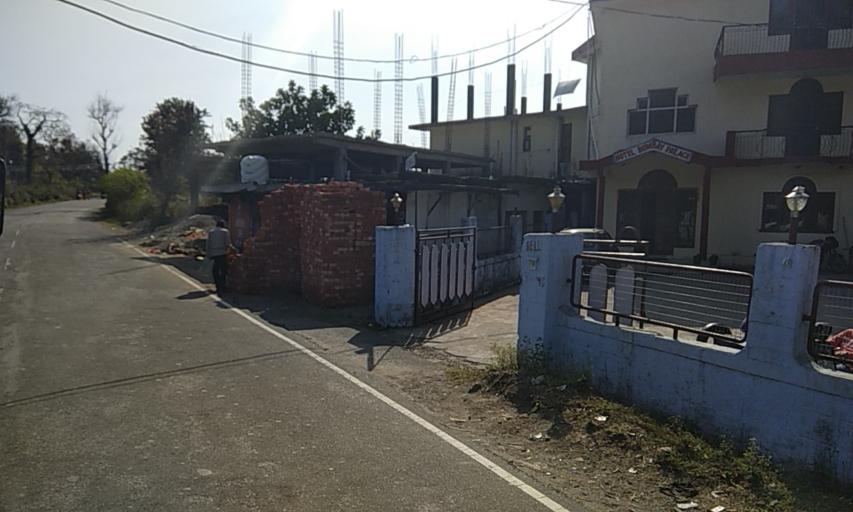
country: IN
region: Himachal Pradesh
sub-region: Kangra
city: Dharmsala
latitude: 32.1532
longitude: 76.4172
